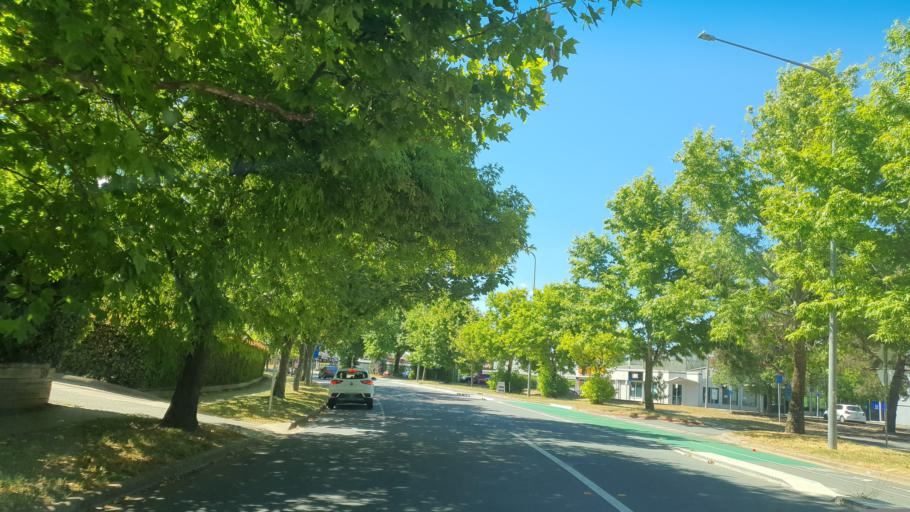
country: AU
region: Australian Capital Territory
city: Macquarie
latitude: -35.2374
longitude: 149.0709
